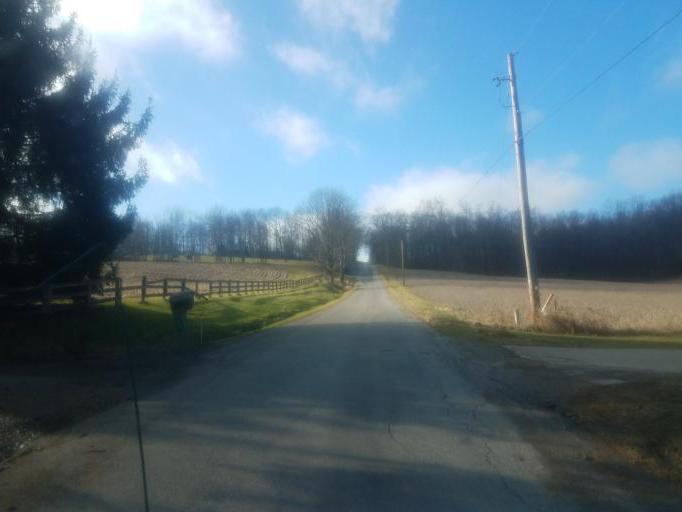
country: US
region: Ohio
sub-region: Sandusky County
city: Bellville
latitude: 40.5827
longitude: -82.5350
